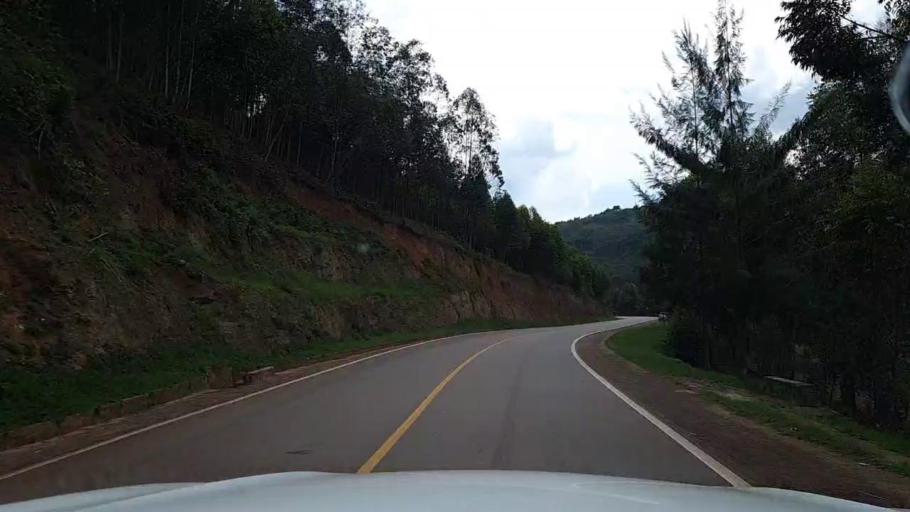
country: RW
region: Kigali
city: Kigali
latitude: -1.8182
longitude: 30.1117
